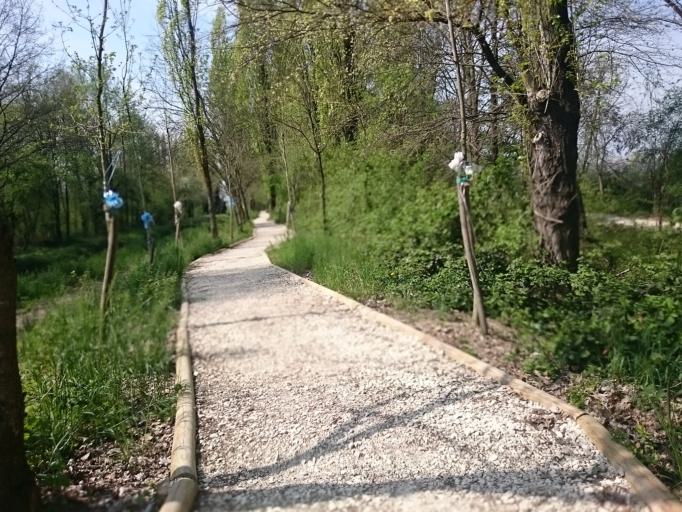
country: IT
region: Veneto
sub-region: Provincia di Padova
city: Bosco
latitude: 45.4377
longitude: 11.7876
